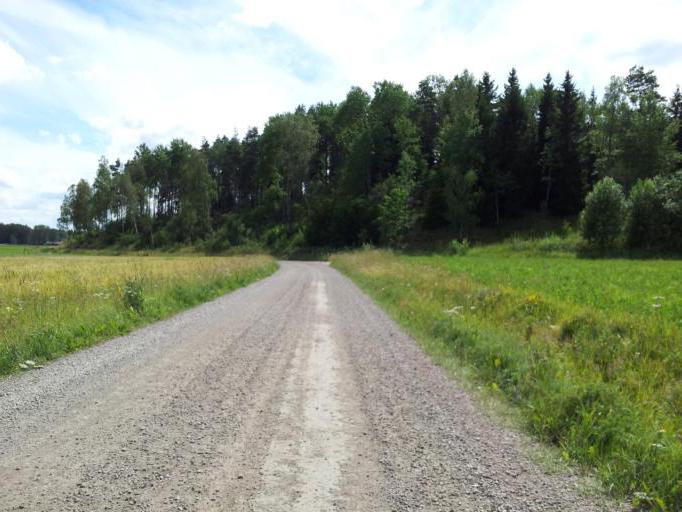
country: SE
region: Stockholm
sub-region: Norrtalje Kommun
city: Nykvarn
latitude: 59.8961
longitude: 18.2154
